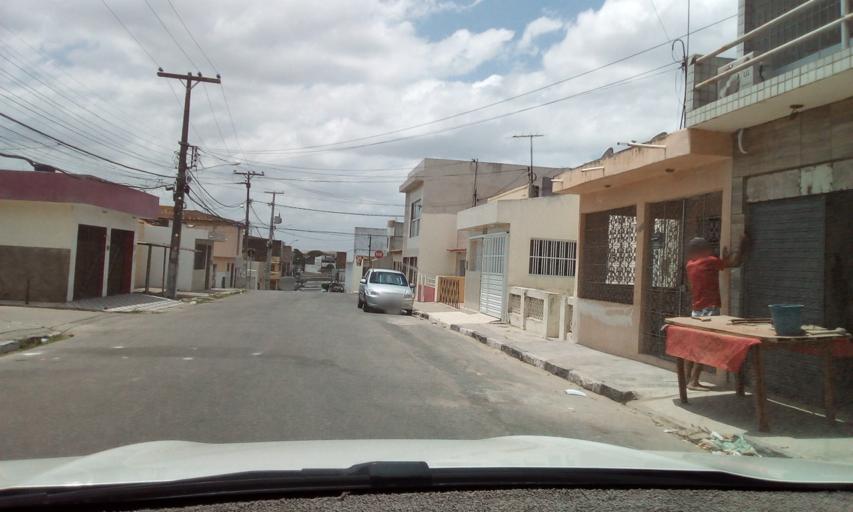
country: BR
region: Pernambuco
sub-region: Caruaru
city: Caruaru
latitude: -8.2726
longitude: -35.9793
